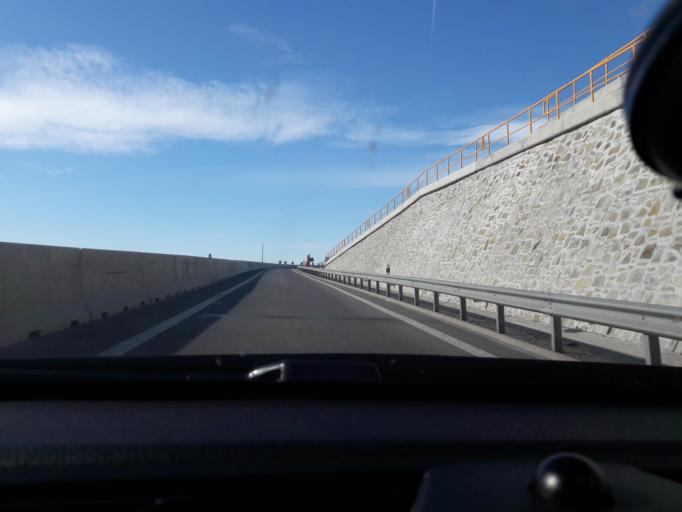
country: SK
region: Banskobystricky
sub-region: Okres Banska Bystrica
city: Zvolen
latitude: 48.5732
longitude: 19.2462
